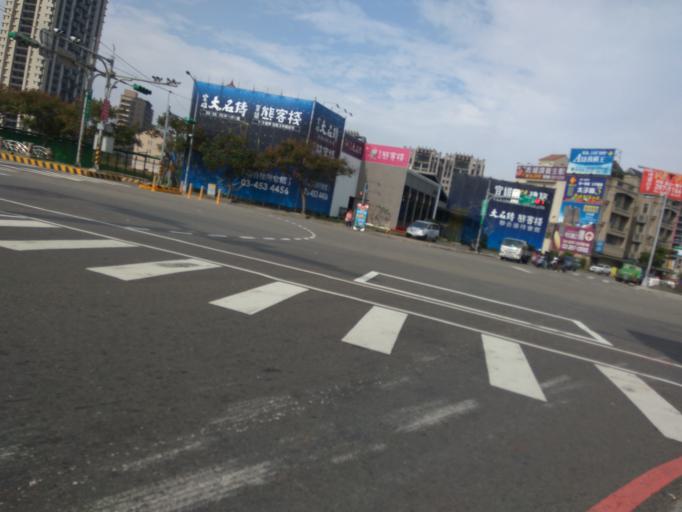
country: TW
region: Taiwan
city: Taoyuan City
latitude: 25.0040
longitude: 121.2140
